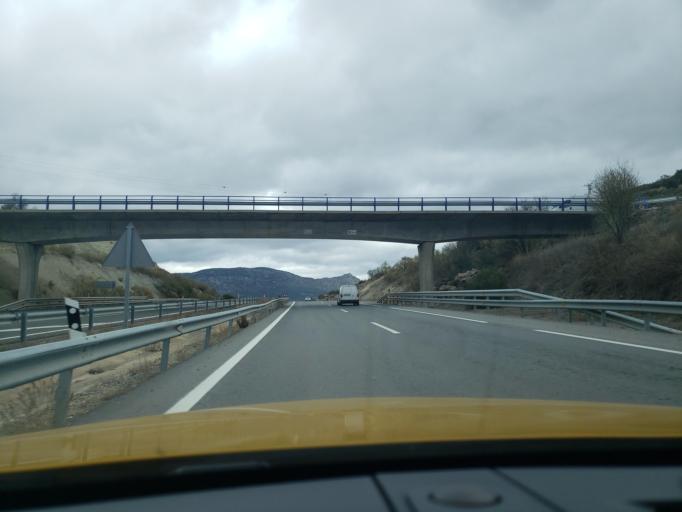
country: ES
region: Andalusia
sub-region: Provincia de Jaen
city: Noalejo
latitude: 37.5318
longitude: -3.6358
